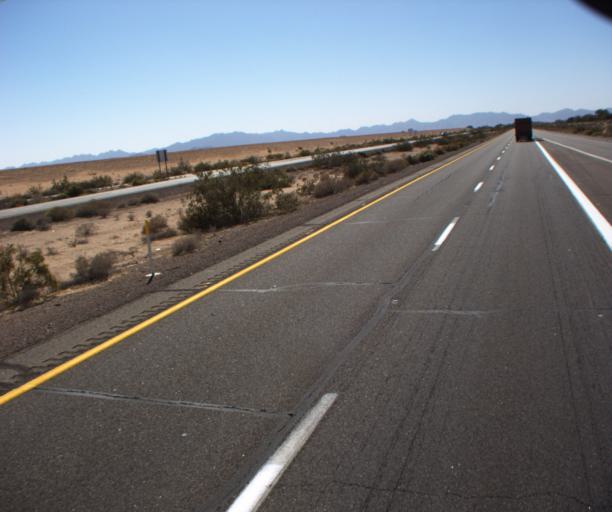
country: US
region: Arizona
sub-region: Yuma County
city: Wellton
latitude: 32.6810
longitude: -114.0255
